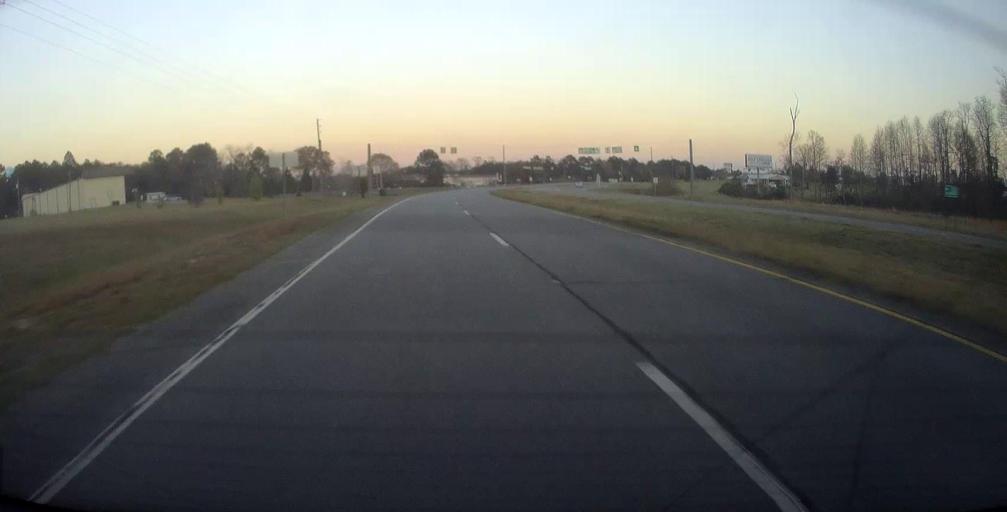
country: US
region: Georgia
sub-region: Dodge County
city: Eastman
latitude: 32.1753
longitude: -83.1639
